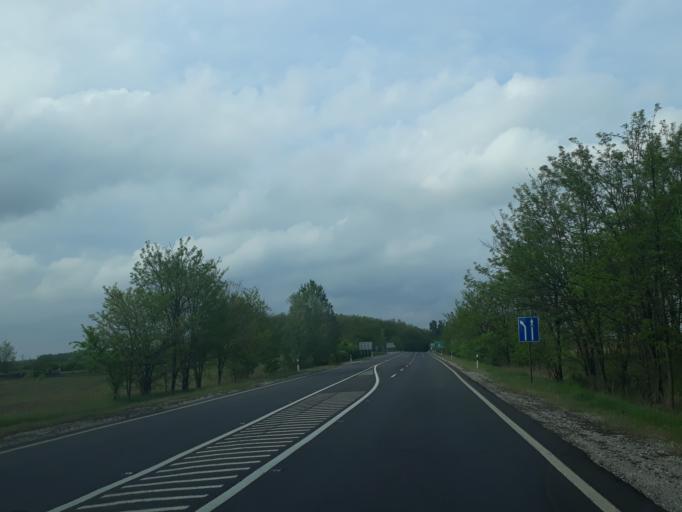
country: HU
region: Szabolcs-Szatmar-Bereg
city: Nyirtass
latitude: 48.1077
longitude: 21.9888
